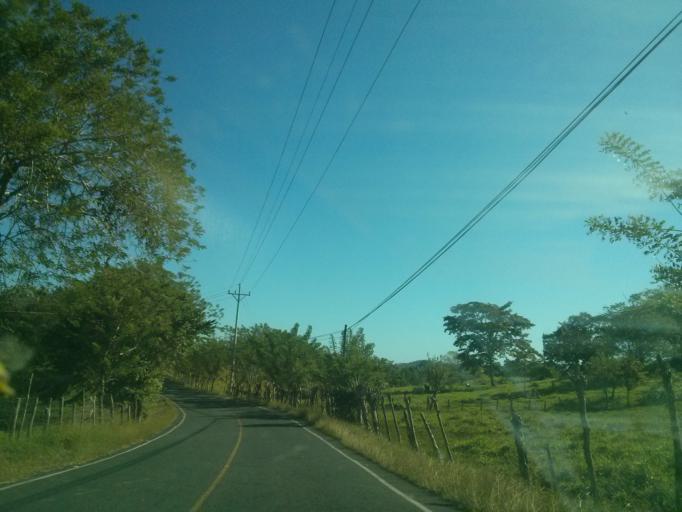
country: CR
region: Puntarenas
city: Paquera
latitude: 9.6996
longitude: -85.0709
